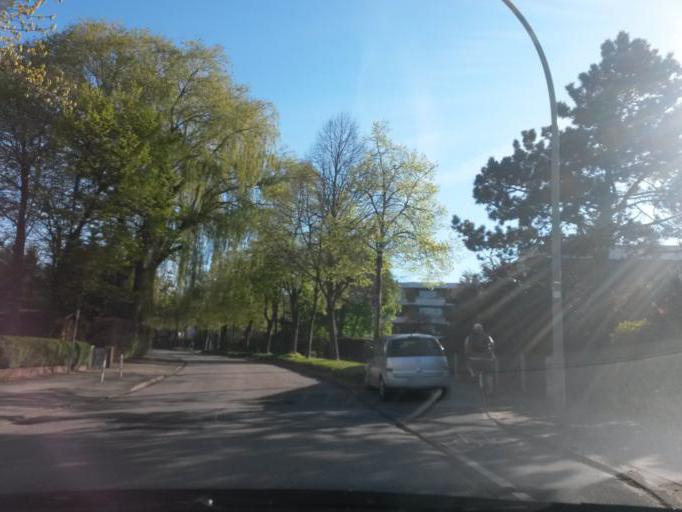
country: DE
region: Schleswig-Holstein
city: Wedel
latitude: 53.5873
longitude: 9.7067
